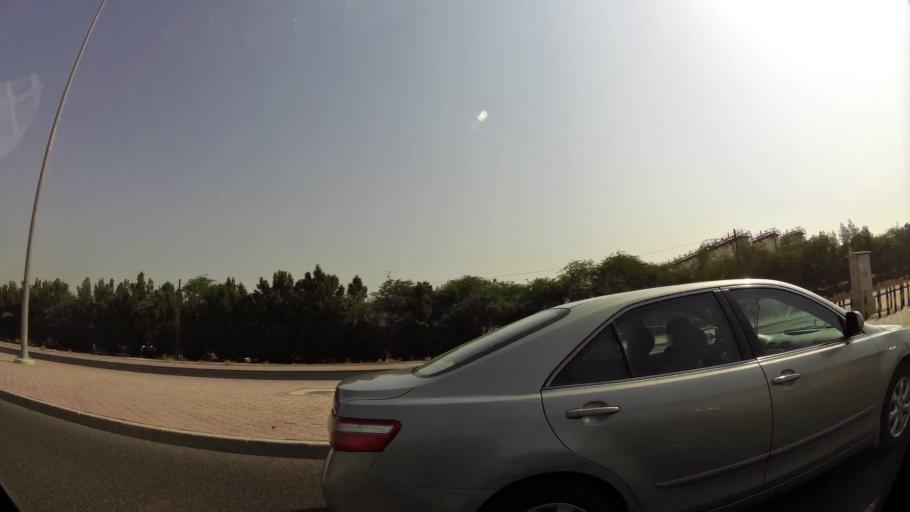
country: KW
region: Al Asimah
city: Ar Rabiyah
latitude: 29.2845
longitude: 47.9144
